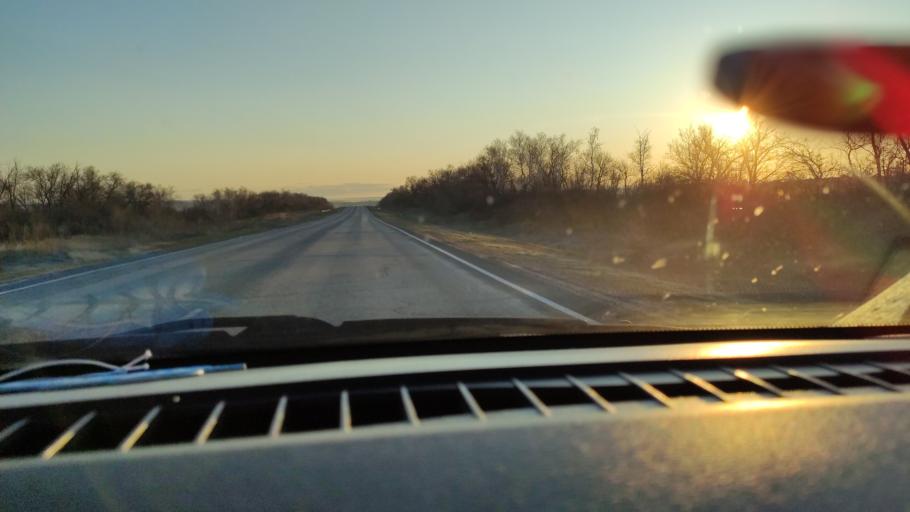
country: RU
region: Saratov
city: Sinodskoye
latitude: 51.9563
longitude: 46.6161
